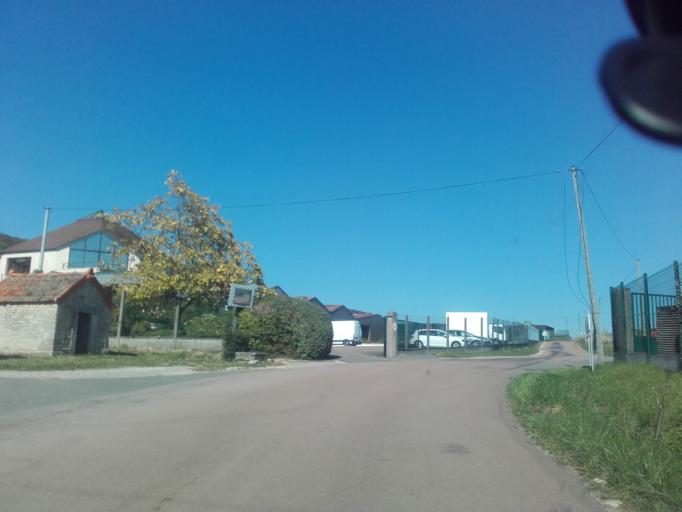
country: FR
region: Bourgogne
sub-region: Departement de la Cote-d'Or
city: Meursault
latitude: 47.0070
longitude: 4.7134
